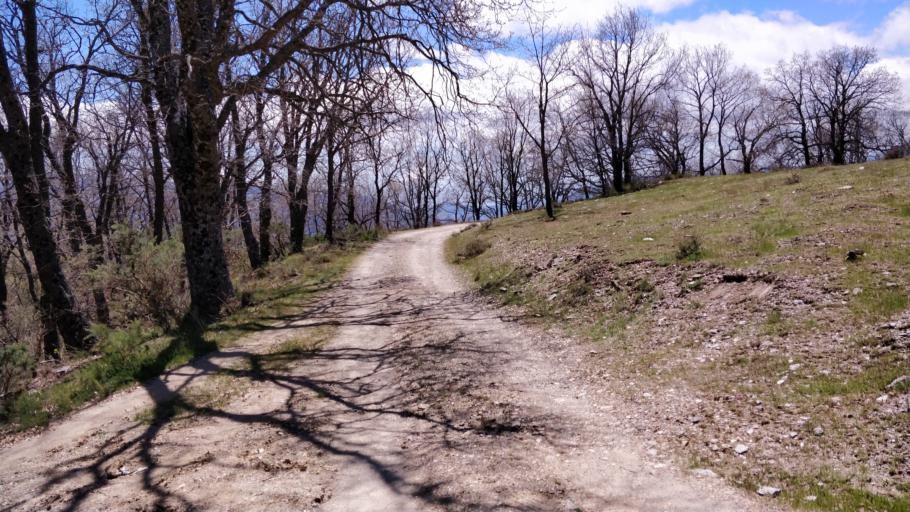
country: ES
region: Andalusia
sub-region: Provincia de Granada
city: Soportujar
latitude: 36.9430
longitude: -3.3898
